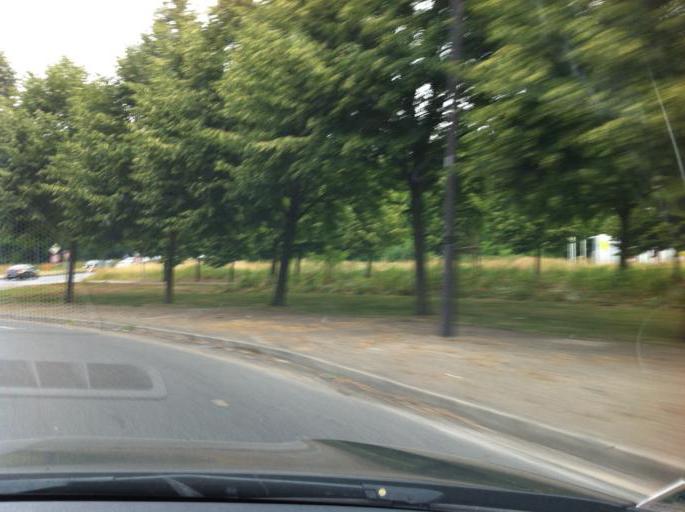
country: FR
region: Ile-de-France
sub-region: Departement de Seine-et-Marne
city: Voisenon
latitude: 48.5528
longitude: 2.6490
